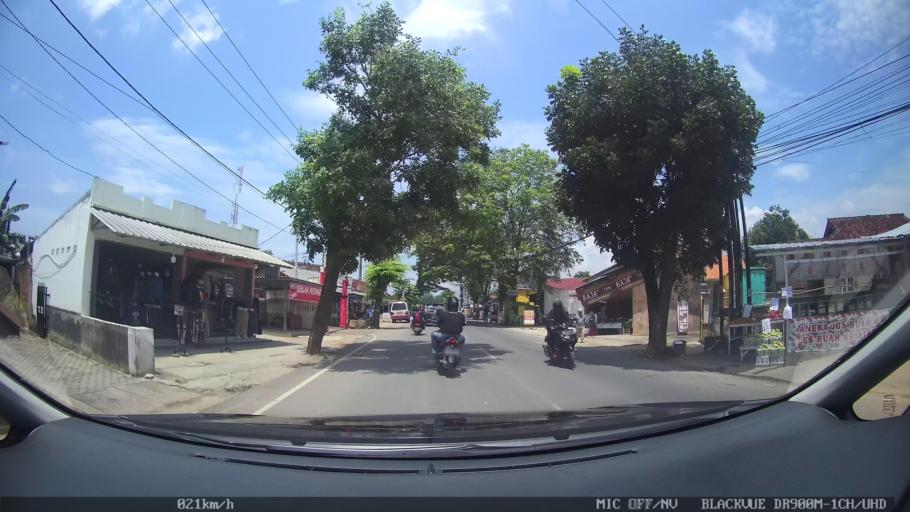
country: ID
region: Lampung
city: Kedaton
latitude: -5.3549
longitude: 105.2891
